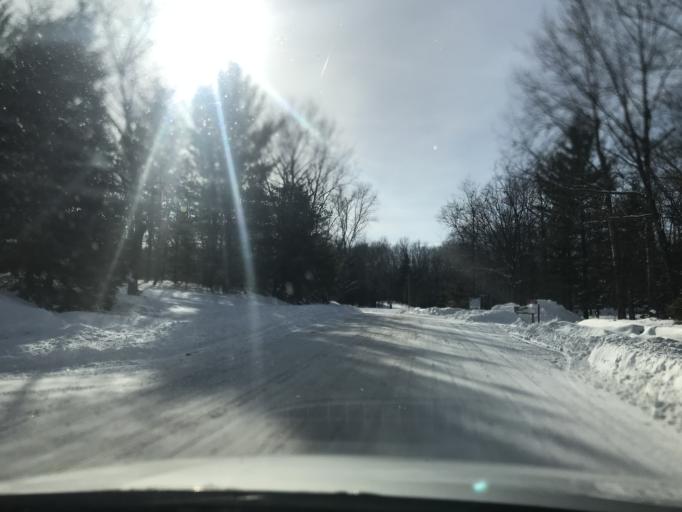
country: US
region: Wisconsin
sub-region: Oconto County
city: Gillett
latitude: 45.1559
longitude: -88.2134
